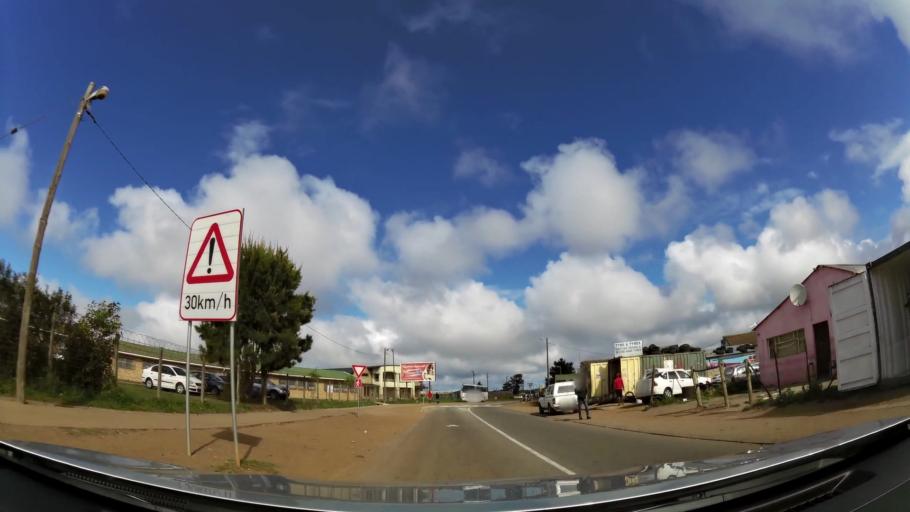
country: ZA
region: Western Cape
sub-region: Eden District Municipality
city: Plettenberg Bay
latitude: -34.0481
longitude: 23.3230
